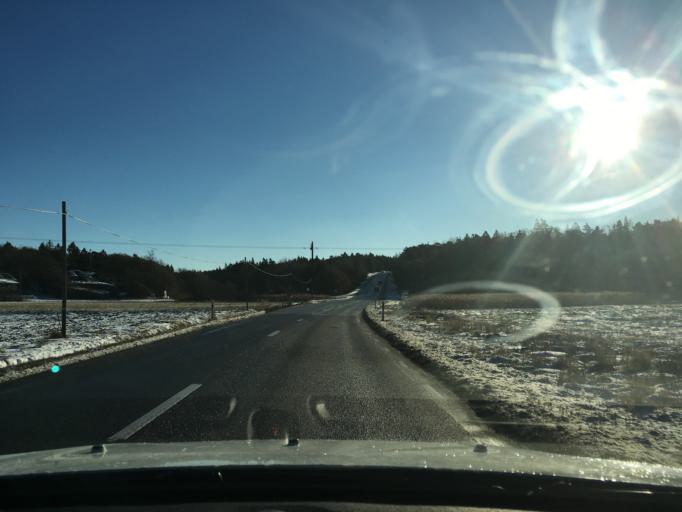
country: SE
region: Vaestra Goetaland
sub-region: Tjorns Kommun
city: Myggenas
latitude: 58.1022
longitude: 11.7070
